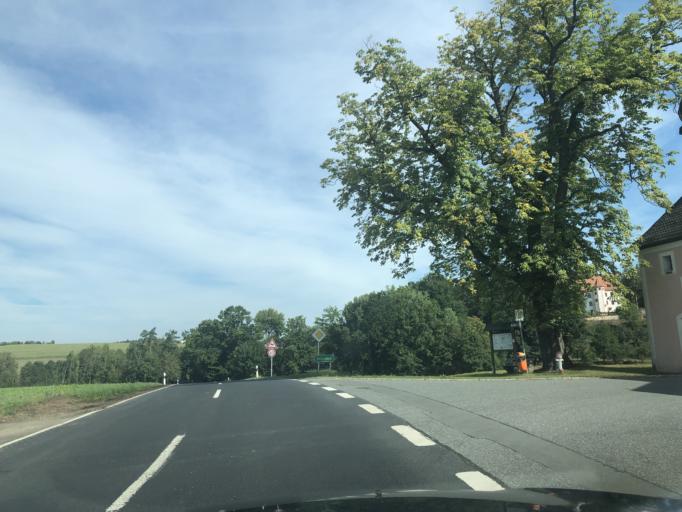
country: DE
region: Bavaria
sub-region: Upper Palatinate
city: Pressath
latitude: 49.7836
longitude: 11.9249
